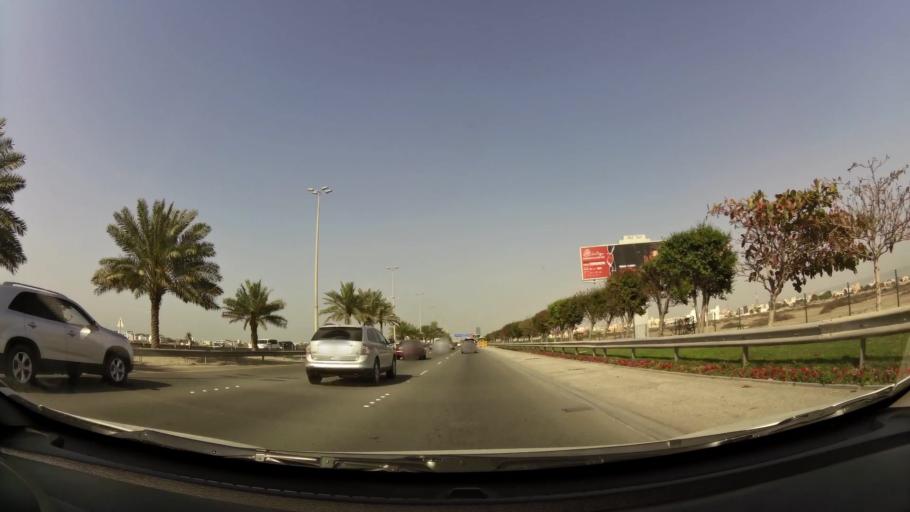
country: BH
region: Manama
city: Jidd Hafs
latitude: 26.2024
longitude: 50.5127
